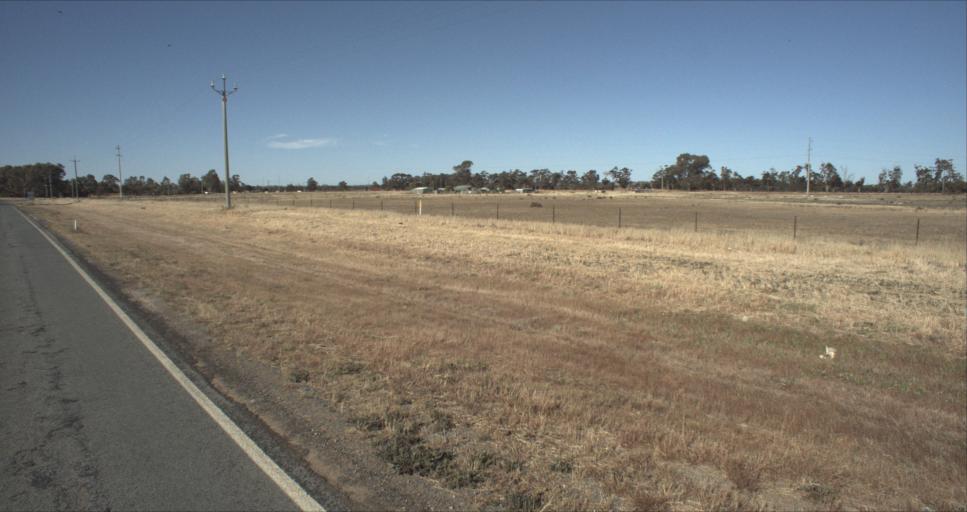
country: AU
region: New South Wales
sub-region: Leeton
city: Leeton
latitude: -34.6124
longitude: 146.4033
